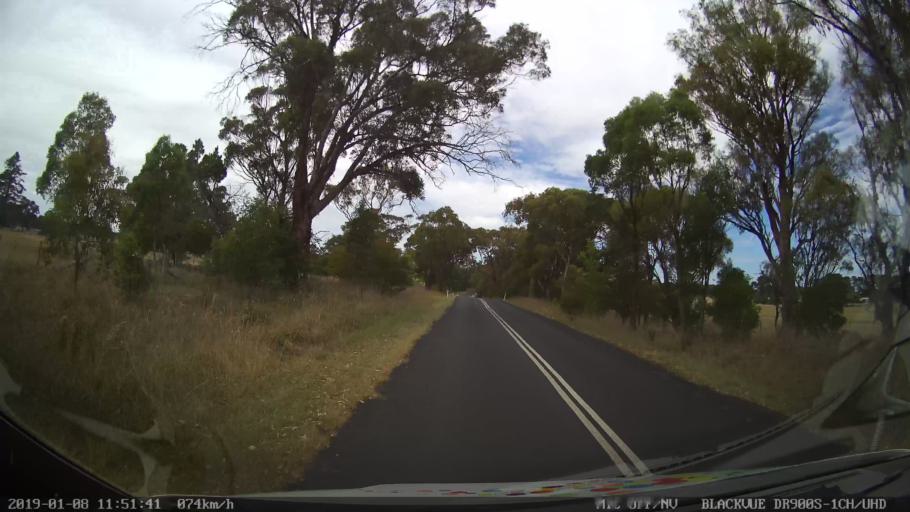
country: AU
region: New South Wales
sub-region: Armidale Dumaresq
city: Armidale
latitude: -30.3956
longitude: 151.5607
